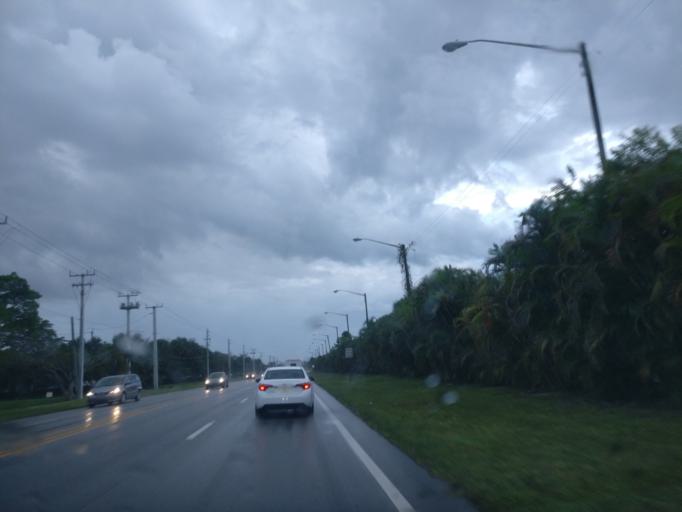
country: US
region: Florida
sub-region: Palm Beach County
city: Schall Circle
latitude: 26.7188
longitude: -80.1189
